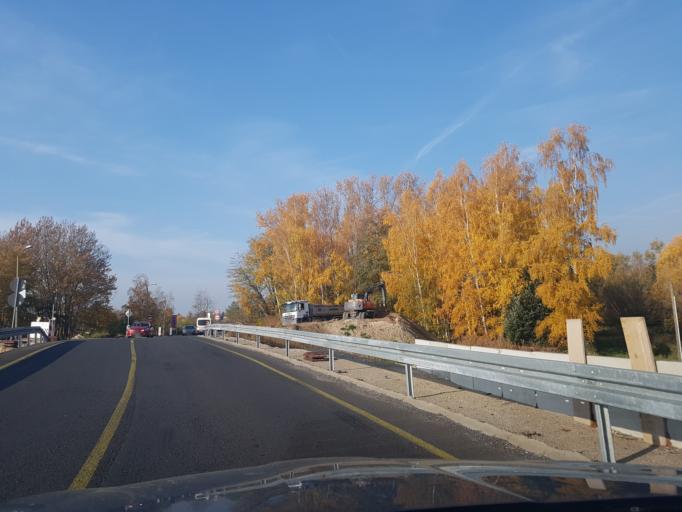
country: DE
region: Brandenburg
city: Elsterwerda
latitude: 51.4638
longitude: 13.5148
